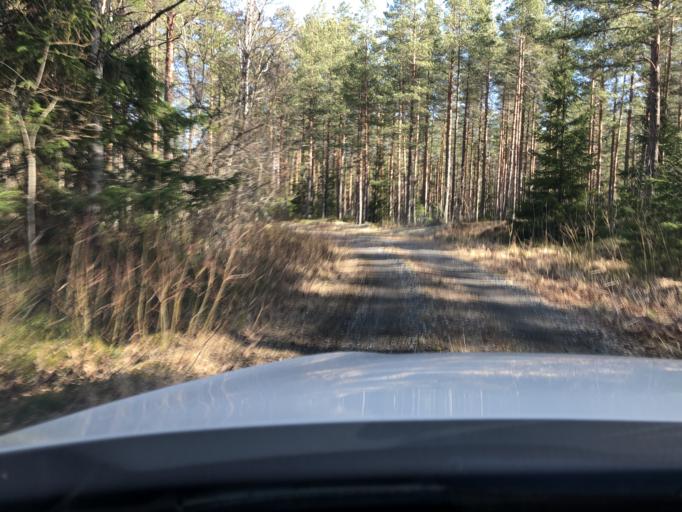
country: SE
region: Uppsala
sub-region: Heby Kommun
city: OEstervala
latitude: 60.3291
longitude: 17.1746
